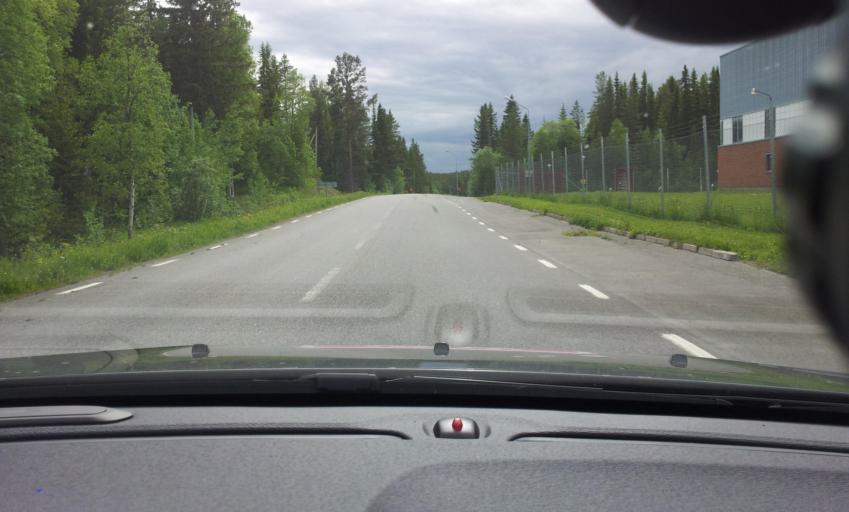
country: SE
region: Jaemtland
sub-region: OEstersunds Kommun
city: Brunflo
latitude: 62.9978
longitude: 14.7402
